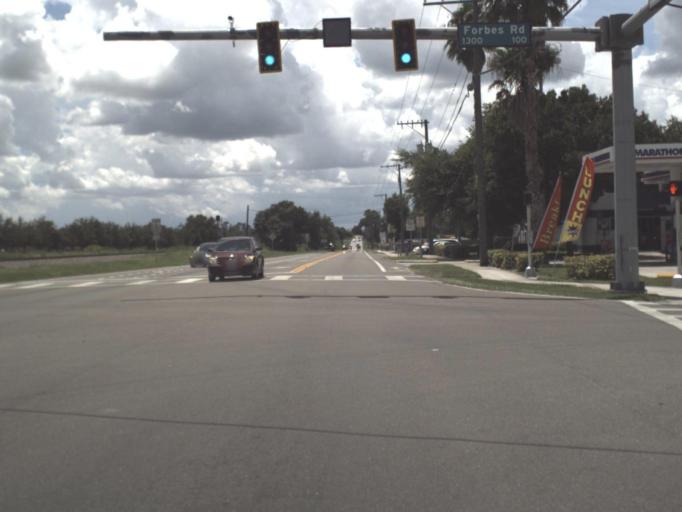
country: US
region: Florida
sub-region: Hillsborough County
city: Dover
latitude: 28.0026
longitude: -82.1867
